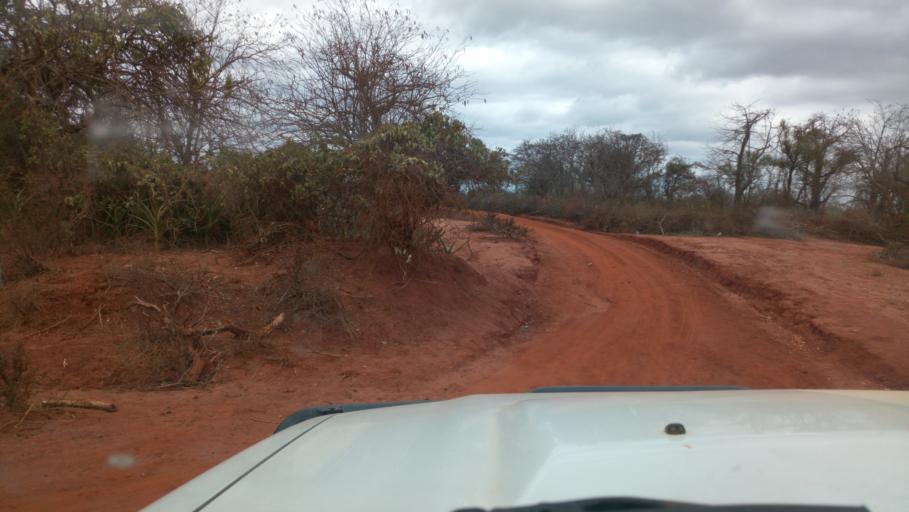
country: KE
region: Kitui
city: Kitui
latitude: -1.9749
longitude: 38.3540
